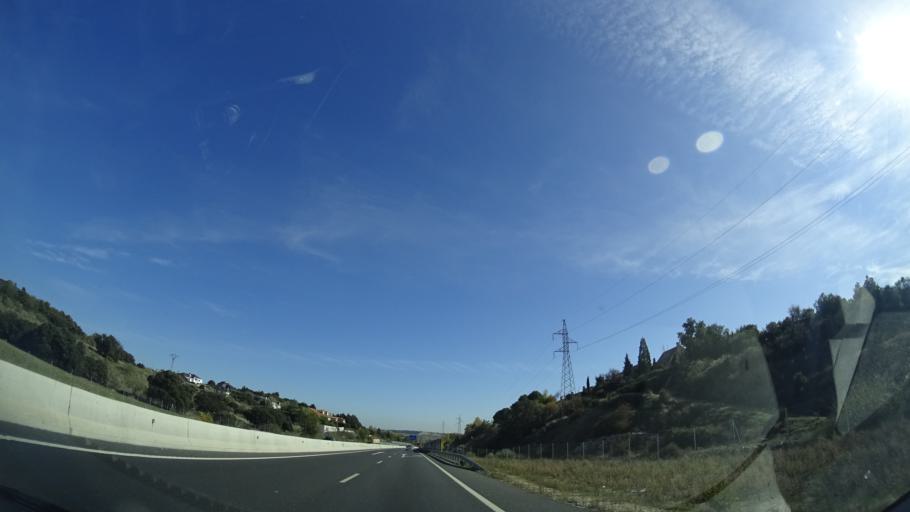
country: ES
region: Madrid
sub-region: Provincia de Madrid
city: Villanueva del Pardillo
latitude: 40.4899
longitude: -3.9518
